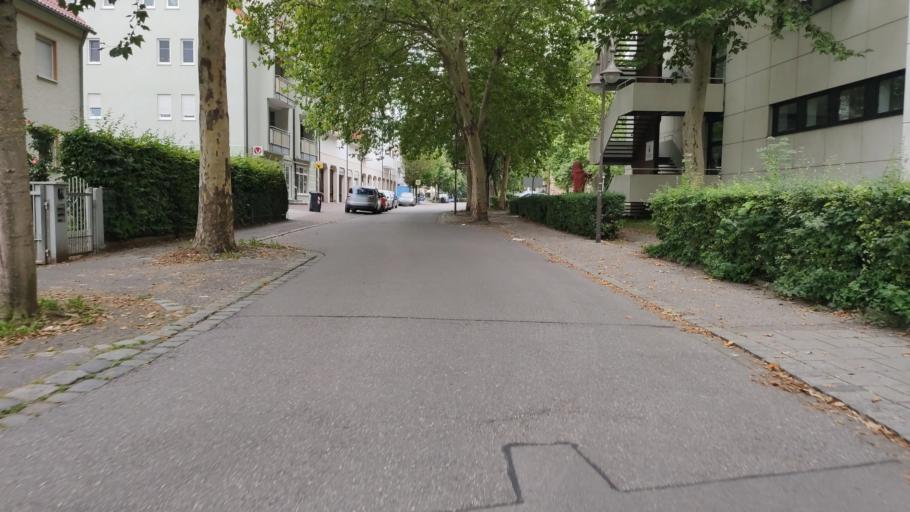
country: DE
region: Bavaria
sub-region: Swabia
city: Konigsbrunn
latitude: 48.2708
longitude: 10.8918
